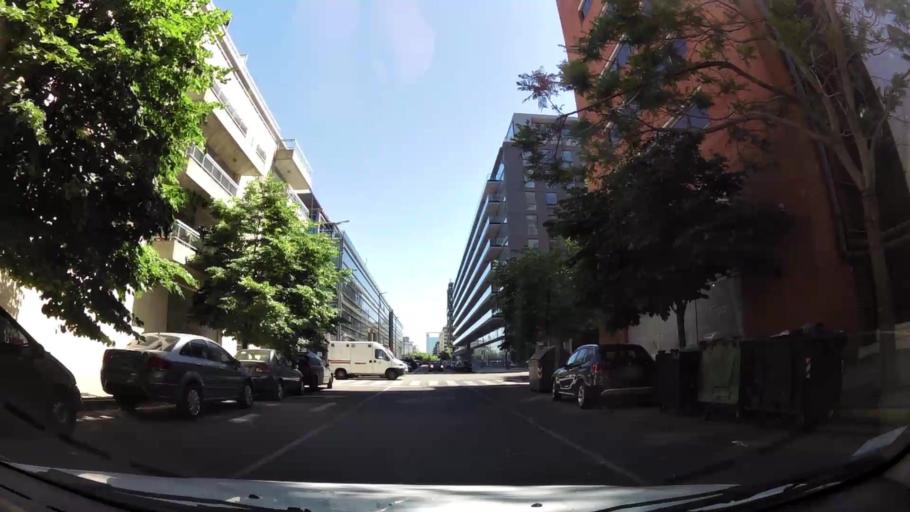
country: AR
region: Buenos Aires F.D.
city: Buenos Aires
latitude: -34.6166
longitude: -58.3630
